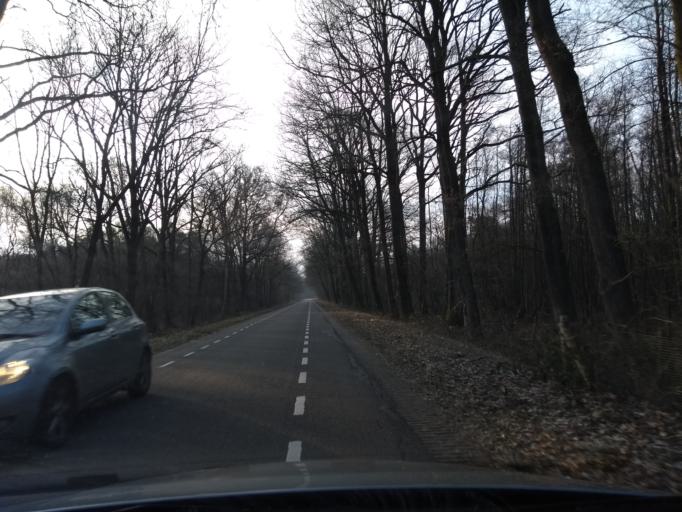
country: NL
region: Overijssel
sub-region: Gemeente Haaksbergen
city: Haaksbergen
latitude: 52.1227
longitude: 6.7483
